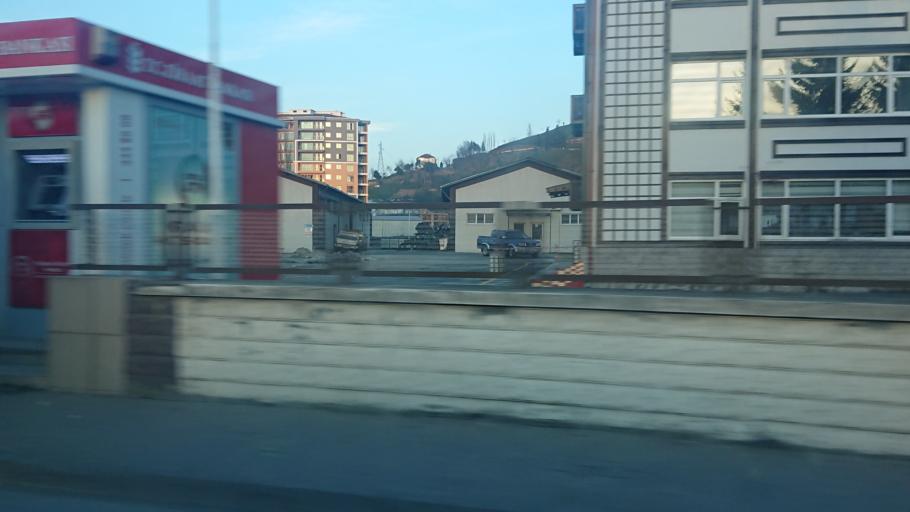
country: TR
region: Rize
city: Gundogdu
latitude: 41.0406
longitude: 40.5793
